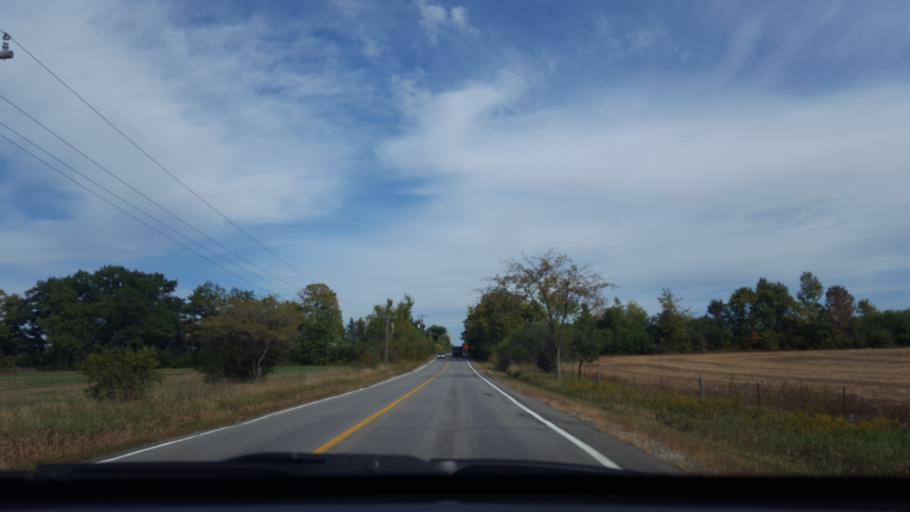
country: CA
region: Ontario
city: Vaughan
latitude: 43.8604
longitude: -79.5793
